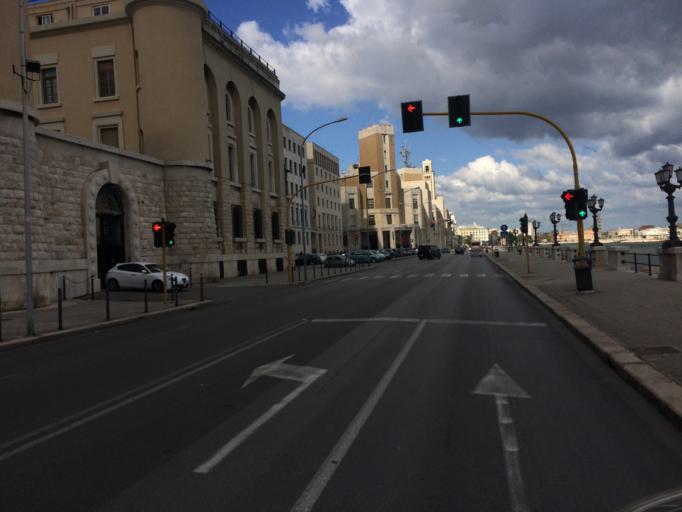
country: IT
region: Apulia
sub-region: Provincia di Bari
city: Bari
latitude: 41.1202
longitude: 16.8862
